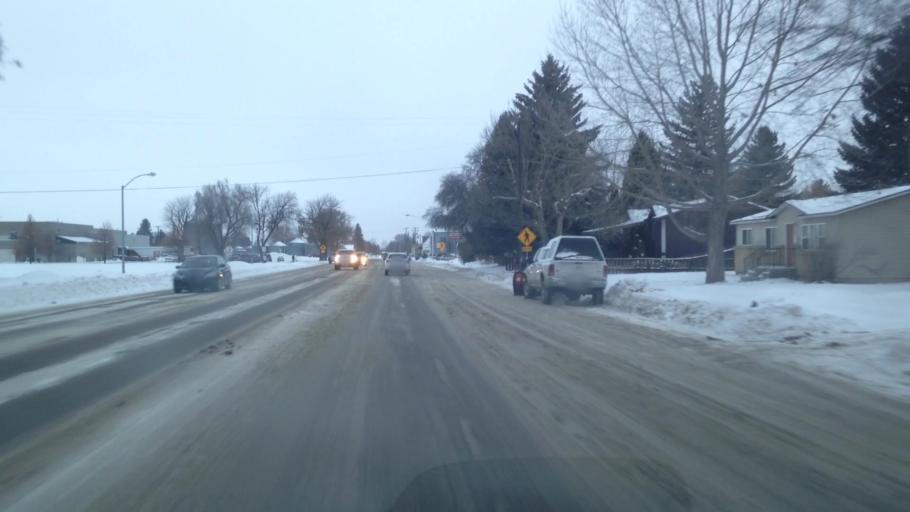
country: US
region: Idaho
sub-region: Madison County
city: Rexburg
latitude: 43.8282
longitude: -111.7845
